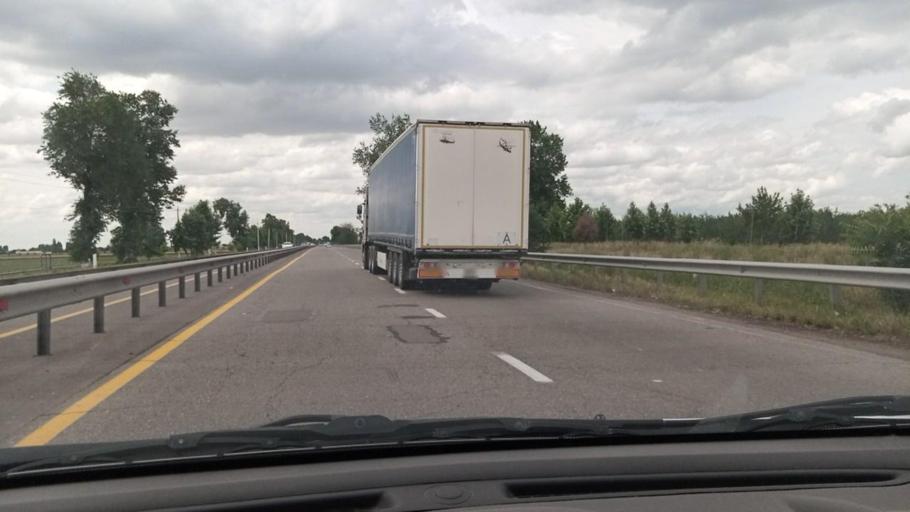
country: UZ
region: Toshkent Shahri
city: Bektemir
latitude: 41.1678
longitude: 69.4159
